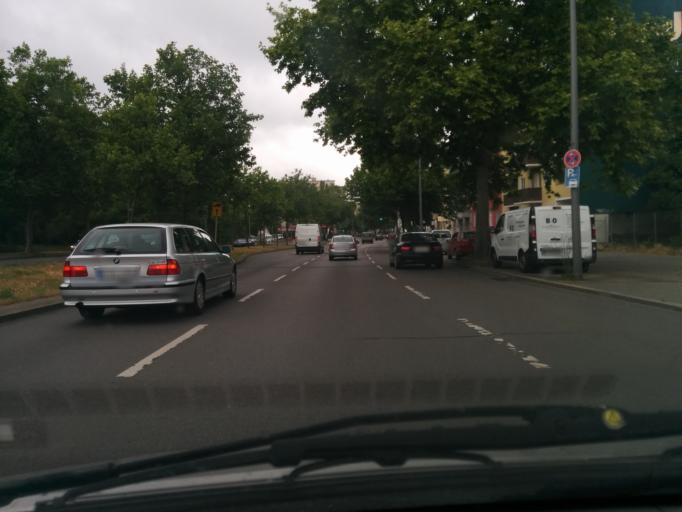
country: DE
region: Berlin
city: Spandau
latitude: 52.5270
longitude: 13.2139
